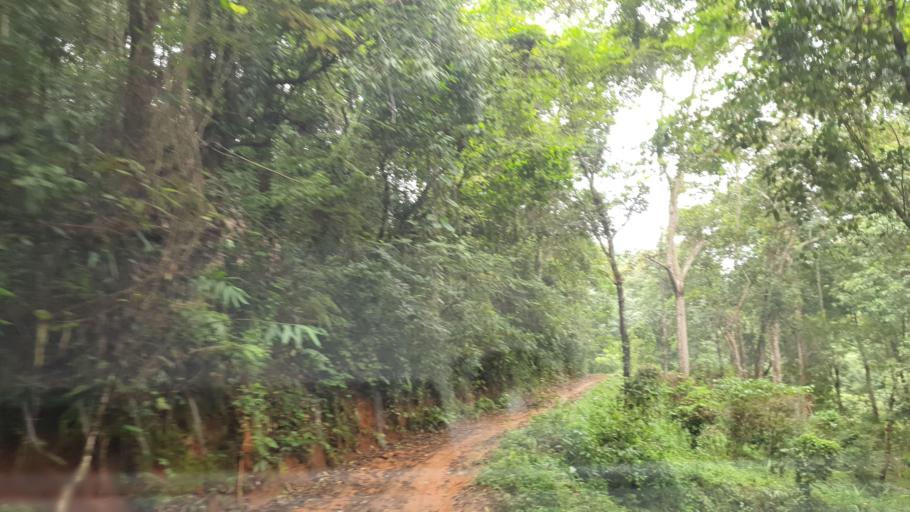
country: TH
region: Chiang Mai
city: Mae On
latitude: 18.9251
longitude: 99.3099
